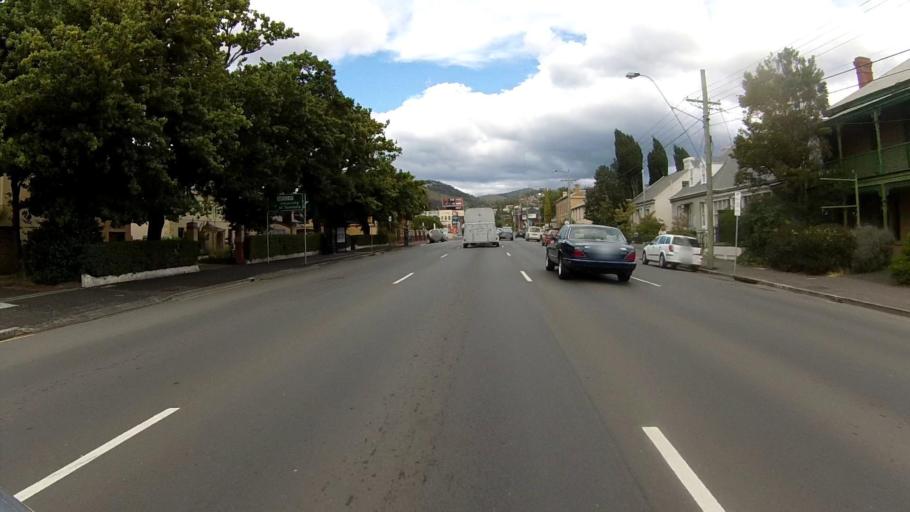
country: AU
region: Tasmania
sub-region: Hobart
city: Sandy Bay
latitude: -42.8902
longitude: 147.3224
